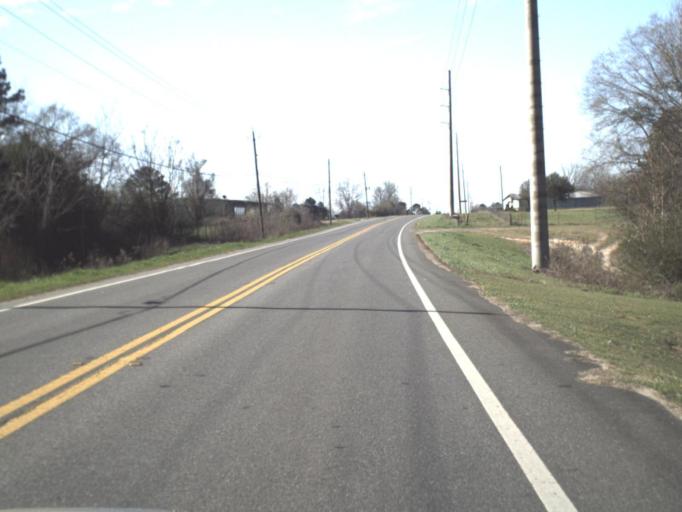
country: US
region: Florida
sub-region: Jackson County
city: Marianna
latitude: 30.7860
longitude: -85.1870
